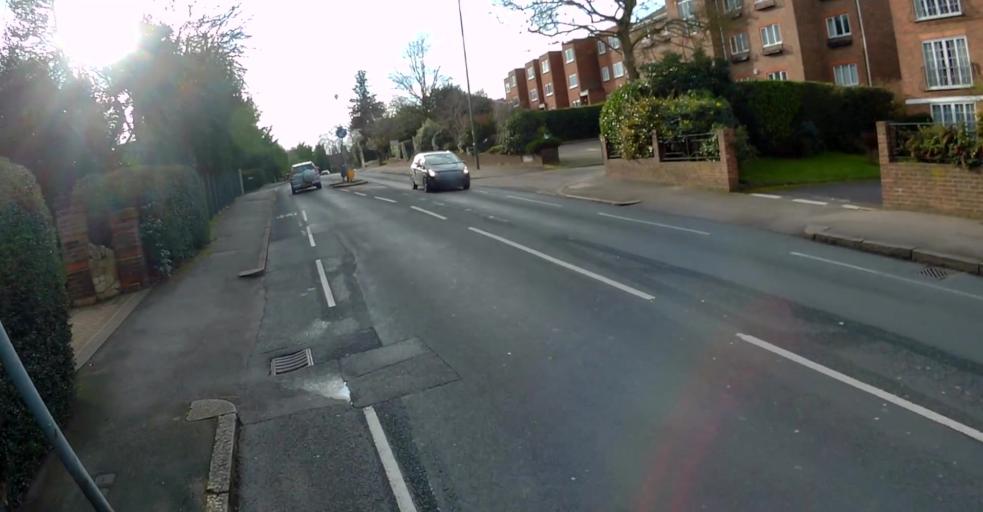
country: GB
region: England
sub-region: Surrey
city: Walton-on-Thames
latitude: 51.3819
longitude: -0.4302
